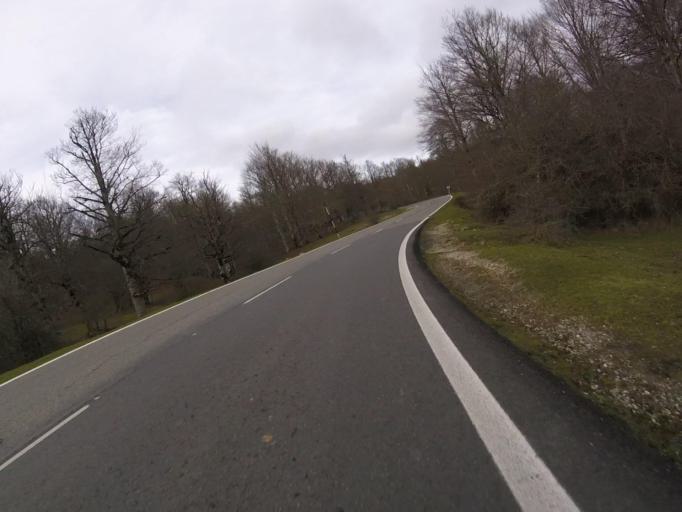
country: ES
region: Navarre
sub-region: Provincia de Navarra
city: Olazagutia
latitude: 42.8363
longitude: -2.1799
